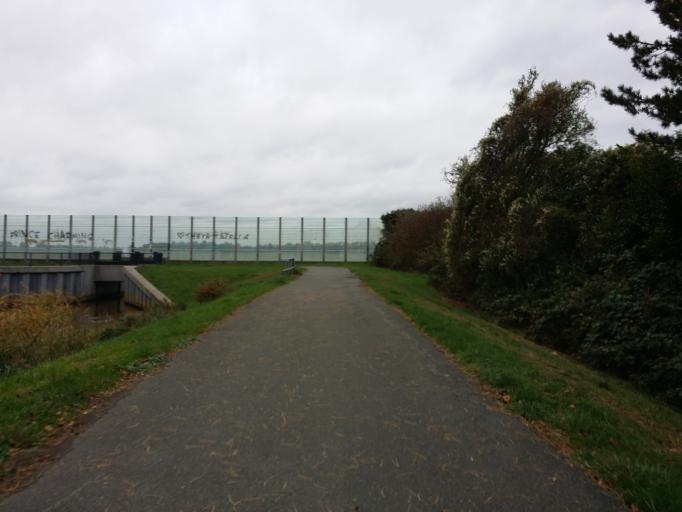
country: DE
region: Lower Saxony
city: Stuhr
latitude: 53.0495
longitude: 8.7711
